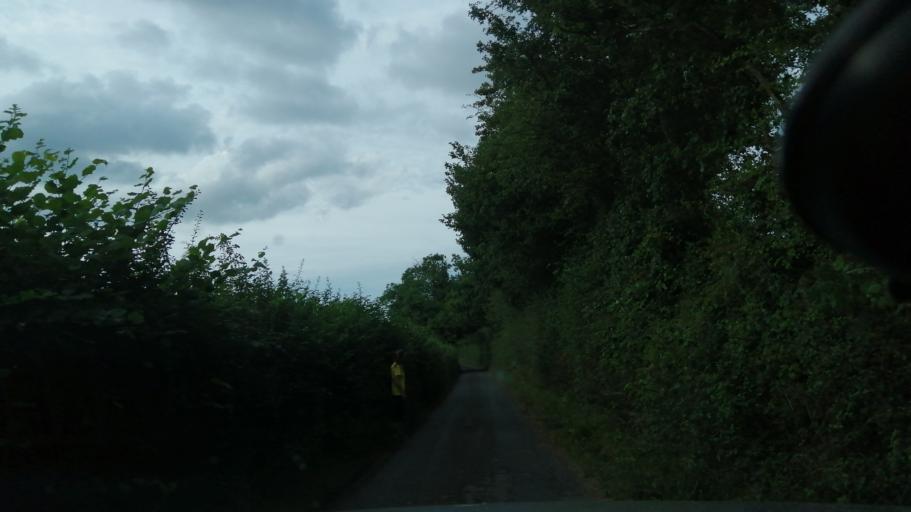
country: GB
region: England
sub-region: Herefordshire
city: Thruxton
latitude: 52.0098
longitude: -2.8030
